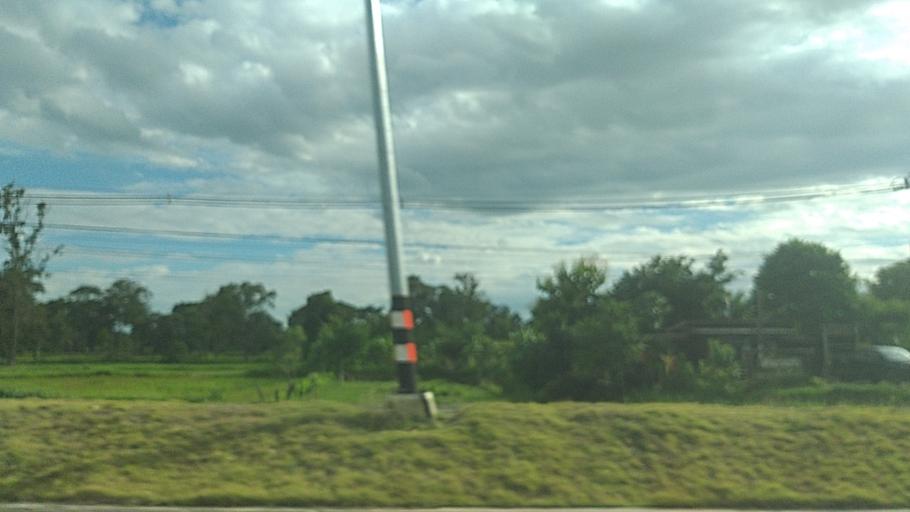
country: TH
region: Surin
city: Prasat
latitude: 14.5826
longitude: 103.4751
